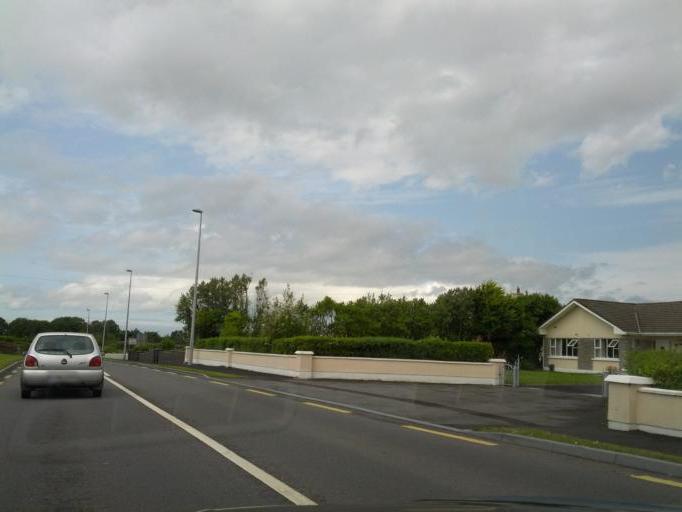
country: IE
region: Munster
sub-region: An Clar
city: Kilrush
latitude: 52.6452
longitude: -9.4937
